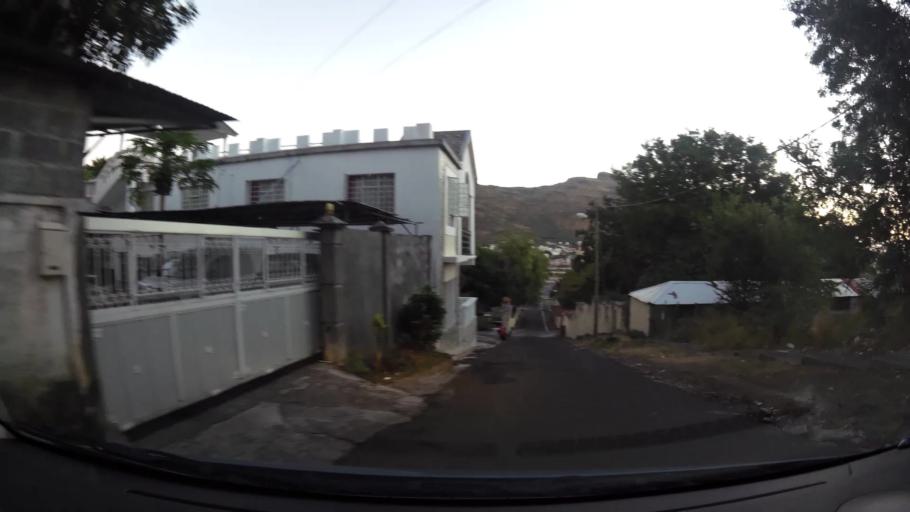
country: MU
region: Port Louis
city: Port Louis
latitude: -20.1671
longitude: 57.5127
